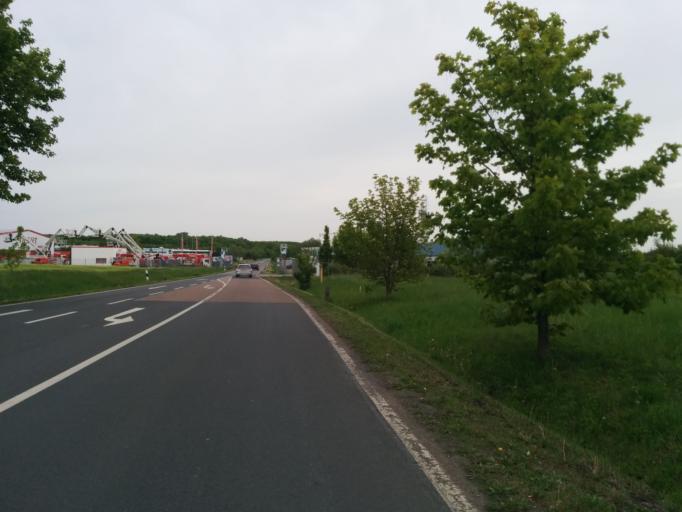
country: DE
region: Saxony-Anhalt
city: Zscherben
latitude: 51.4703
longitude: 11.8785
